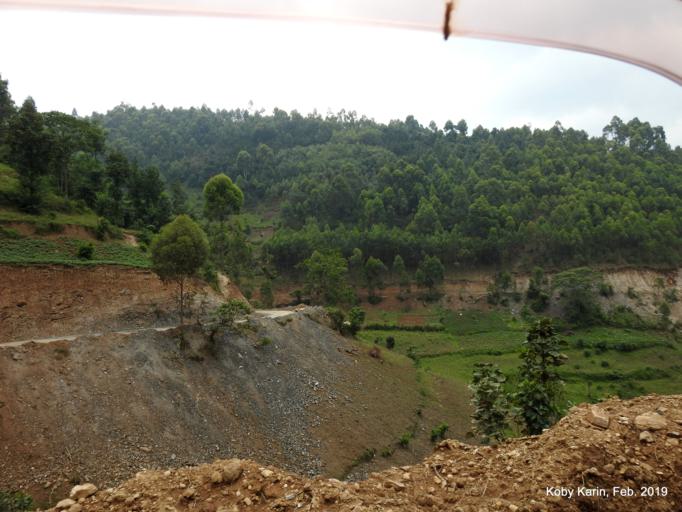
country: UG
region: Western Region
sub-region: Kisoro District
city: Kisoro
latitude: -1.1427
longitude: 29.7418
